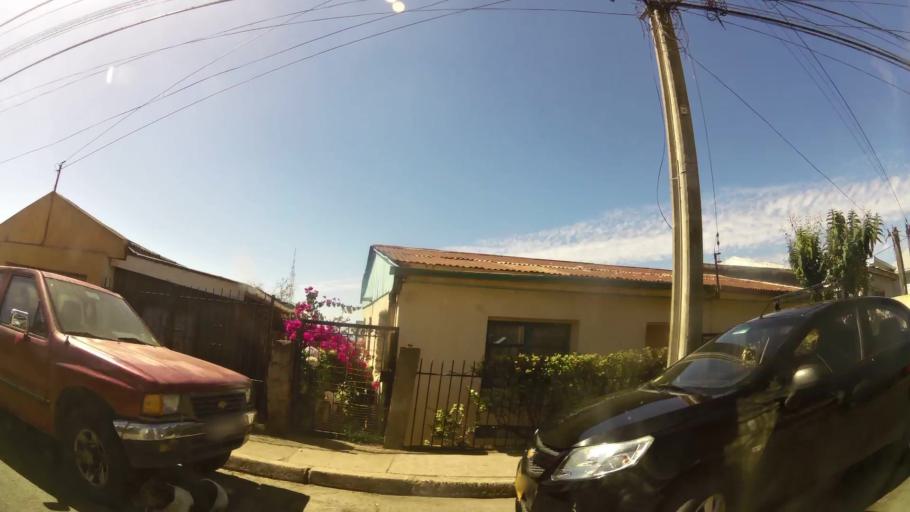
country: CL
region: Valparaiso
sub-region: Provincia de Valparaiso
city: Vina del Mar
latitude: -33.0419
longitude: -71.5675
